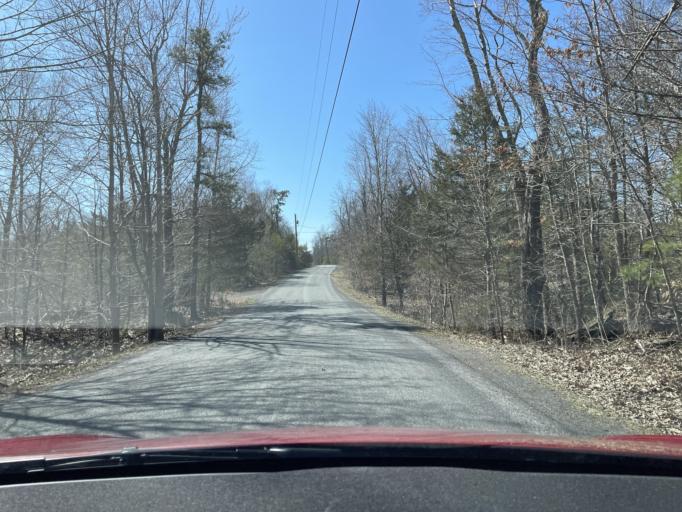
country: US
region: New York
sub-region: Ulster County
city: Zena
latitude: 42.0569
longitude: -74.0254
